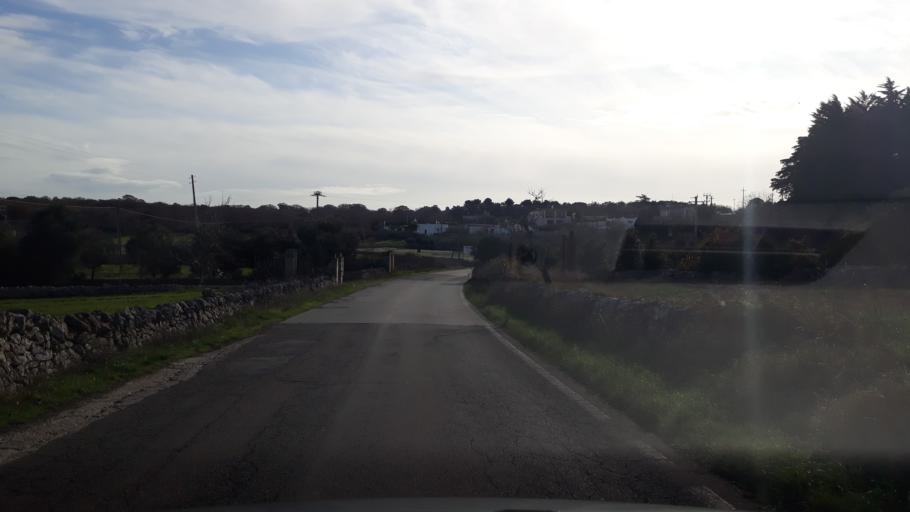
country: IT
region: Apulia
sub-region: Provincia di Taranto
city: Martina Franca
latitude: 40.6804
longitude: 17.3555
